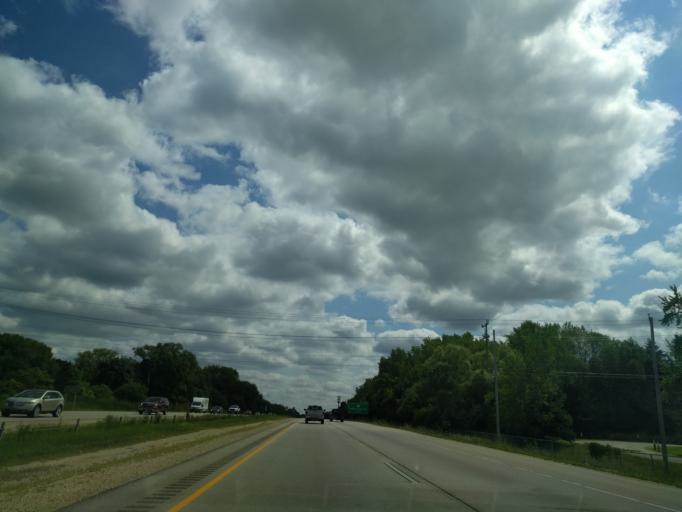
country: US
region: Wisconsin
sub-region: Milwaukee County
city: River Hills
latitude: 43.1629
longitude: -87.9159
